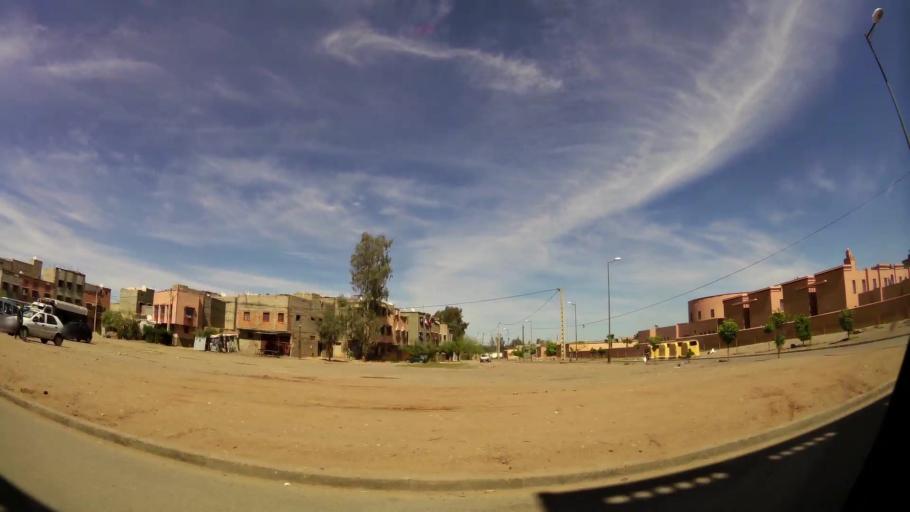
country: MA
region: Marrakech-Tensift-Al Haouz
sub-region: Marrakech
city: Marrakesh
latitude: 31.5988
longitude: -7.9604
